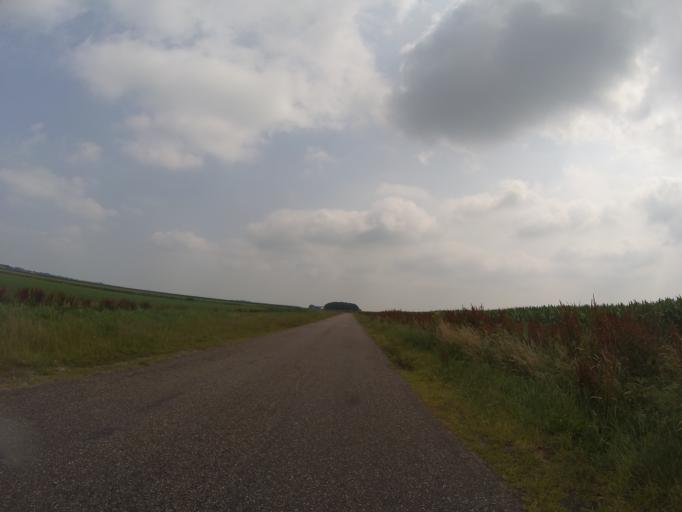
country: NL
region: Drenthe
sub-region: Gemeente Emmen
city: Emmen
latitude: 52.8512
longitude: 6.9276
